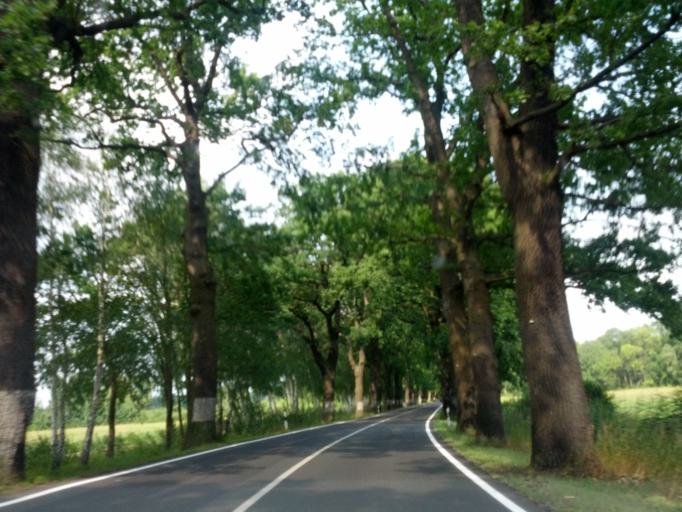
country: DE
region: Brandenburg
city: Nauen
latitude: 52.6603
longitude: 12.9230
